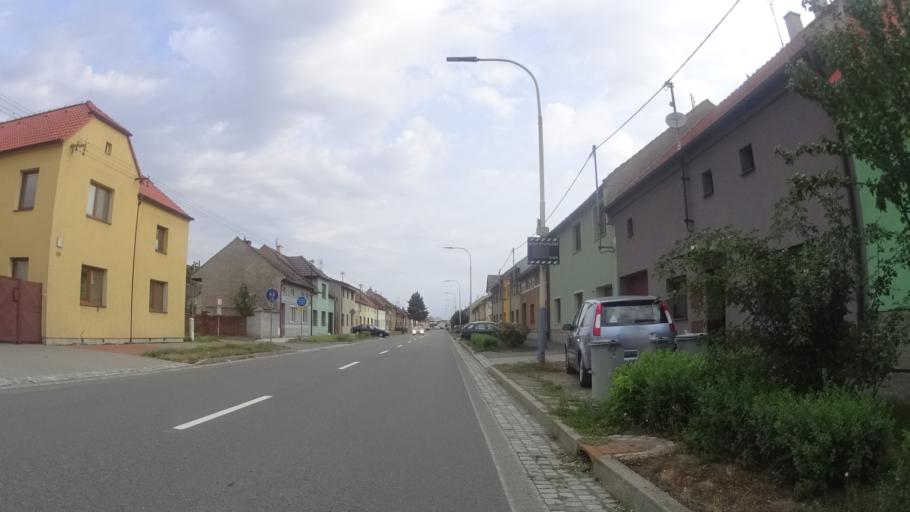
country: CZ
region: Zlin
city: Chropyne
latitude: 49.3511
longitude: 17.3750
